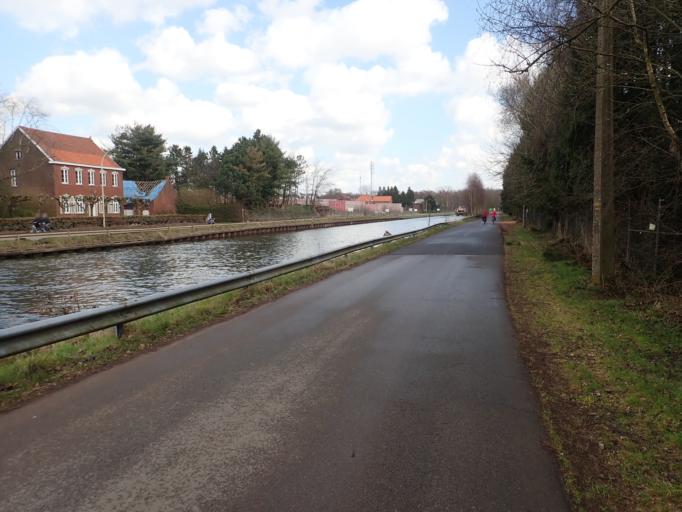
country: BE
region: Flanders
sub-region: Provincie Antwerpen
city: Vosselaar
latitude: 51.3300
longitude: 4.8769
